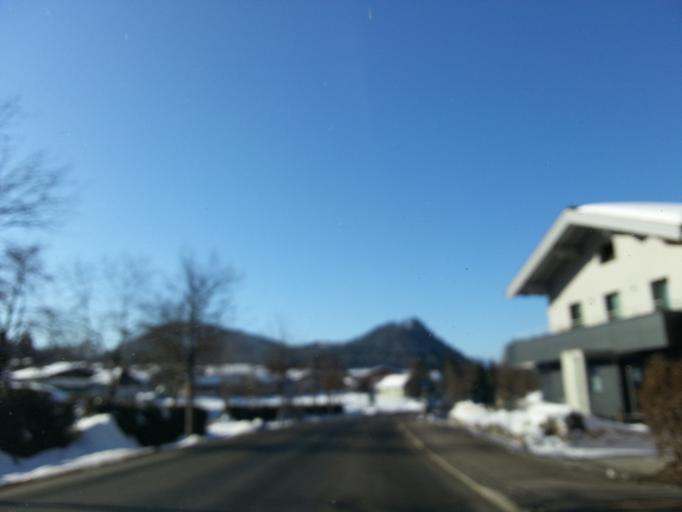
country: AT
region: Salzburg
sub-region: Politischer Bezirk Sankt Johann im Pongau
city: Eben im Pongau
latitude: 47.4631
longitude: 13.3805
